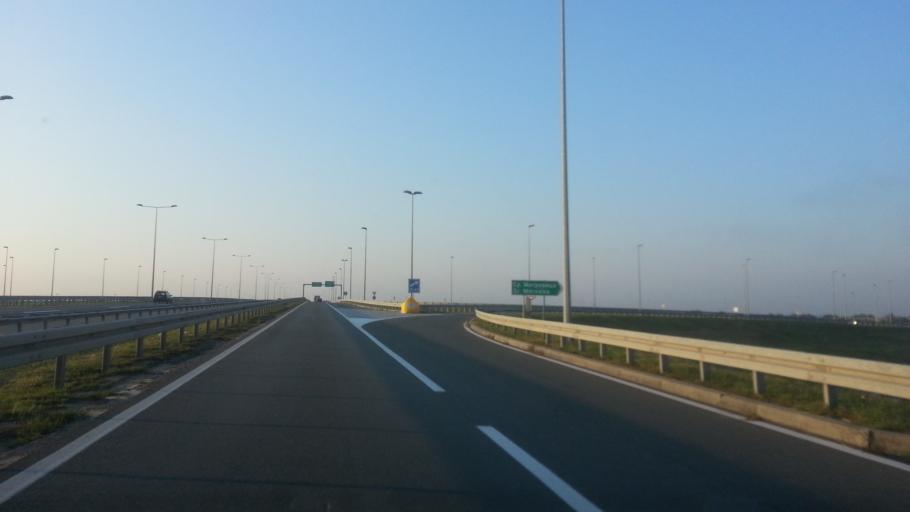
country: RS
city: Dobanovci
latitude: 44.8392
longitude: 20.2501
